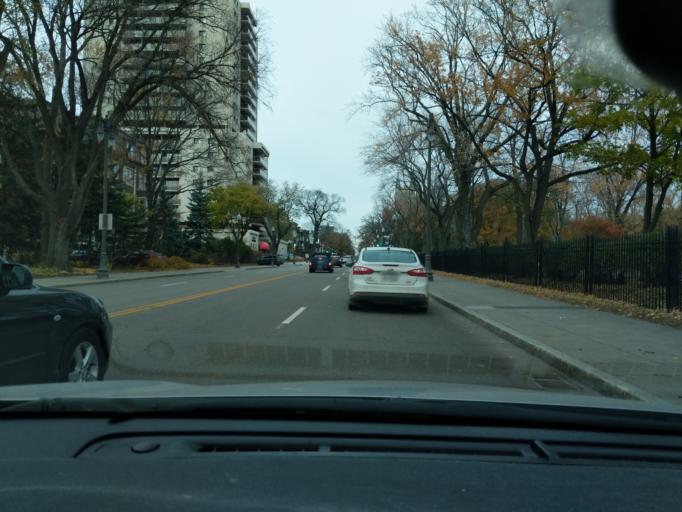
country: CA
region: Quebec
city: Quebec
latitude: 46.7998
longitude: -71.2278
